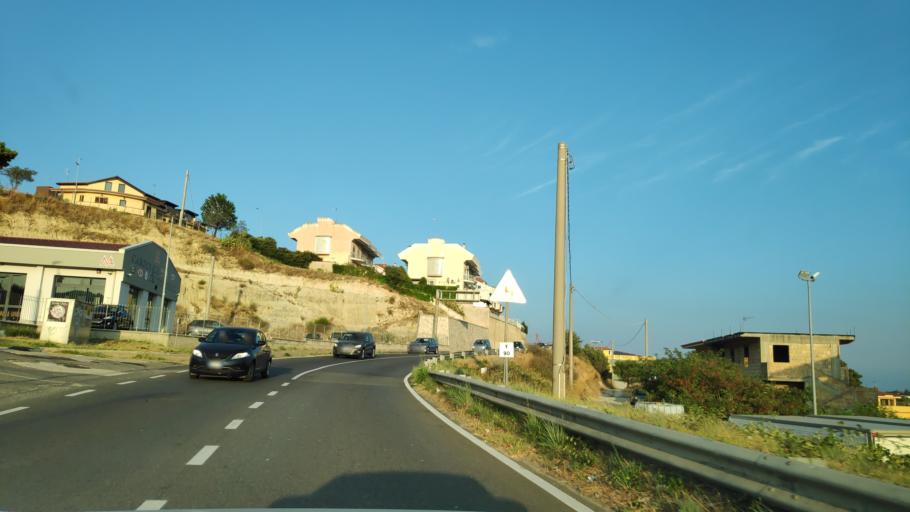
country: IT
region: Calabria
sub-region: Provincia di Catanzaro
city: Martelli-Laganosa
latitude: 38.6792
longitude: 16.5358
